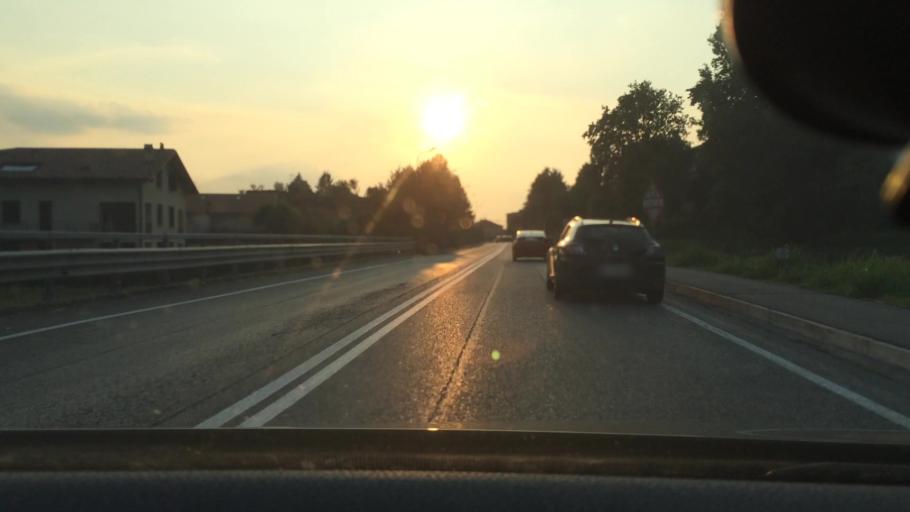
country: IT
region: Lombardy
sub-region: Provincia di Lecco
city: Rovagnate
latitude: 45.7360
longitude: 9.3795
